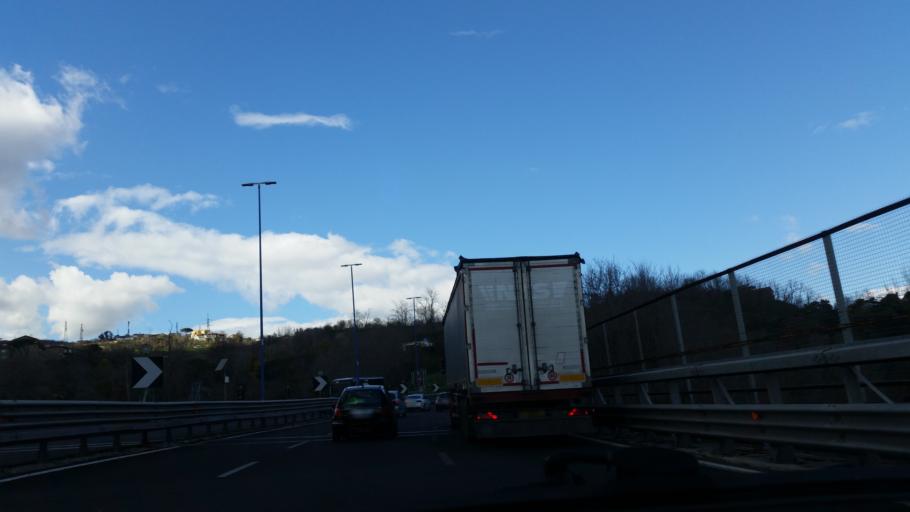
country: IT
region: Campania
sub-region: Provincia di Napoli
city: Napoli
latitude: 40.8497
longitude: 14.2149
